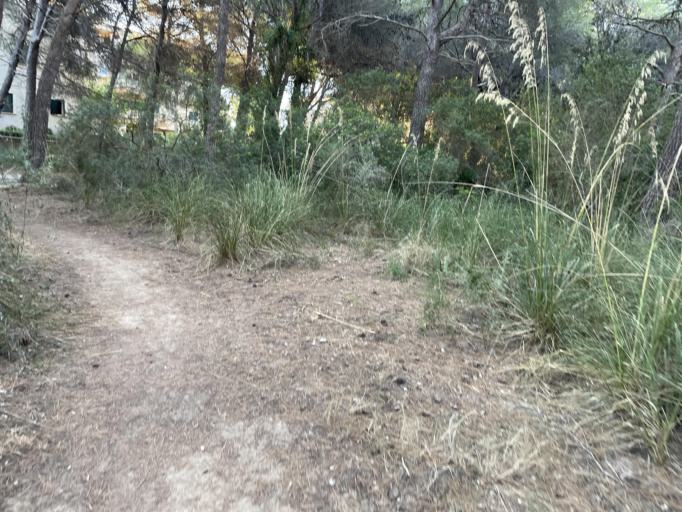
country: ES
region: Balearic Islands
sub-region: Illes Balears
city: Capdepera
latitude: 39.7173
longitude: 3.4554
